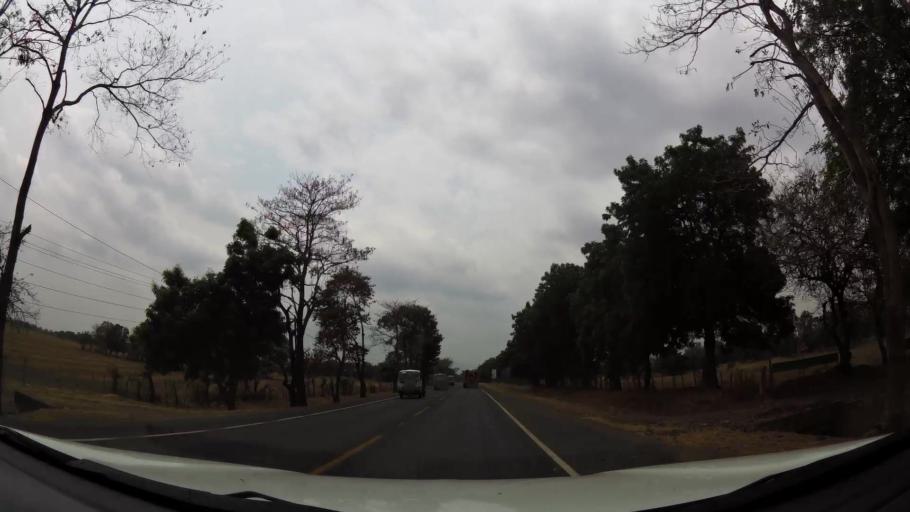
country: NI
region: Leon
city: Telica
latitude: 12.4993
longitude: -86.8600
